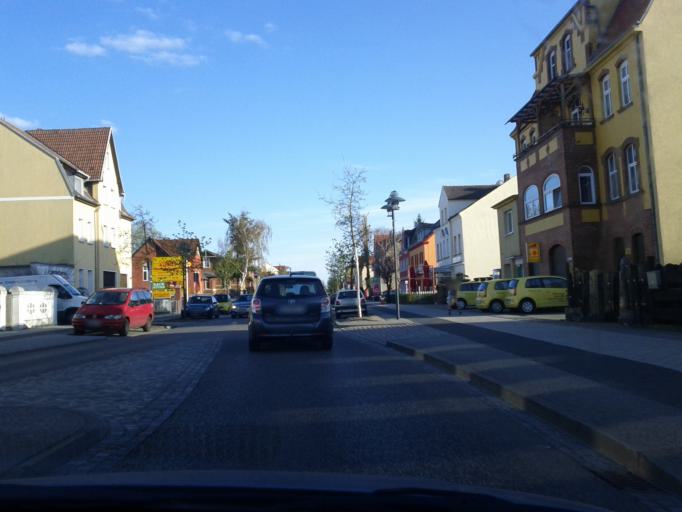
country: DE
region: Brandenburg
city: Furstenwalde
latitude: 52.3486
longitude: 14.0698
